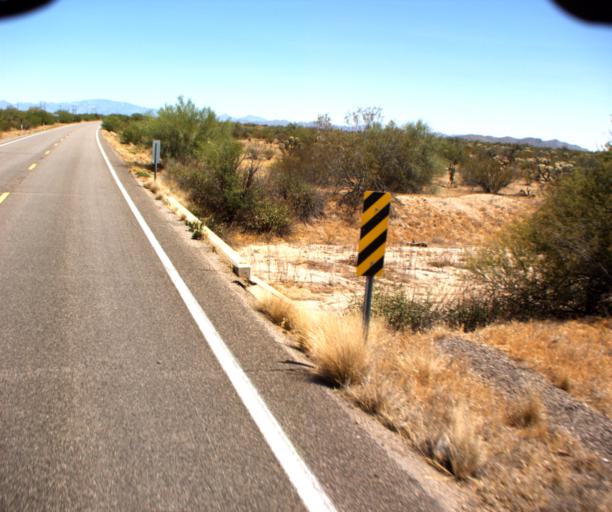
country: US
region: Arizona
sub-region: Pima County
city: Catalina
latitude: 32.7499
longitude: -111.1326
